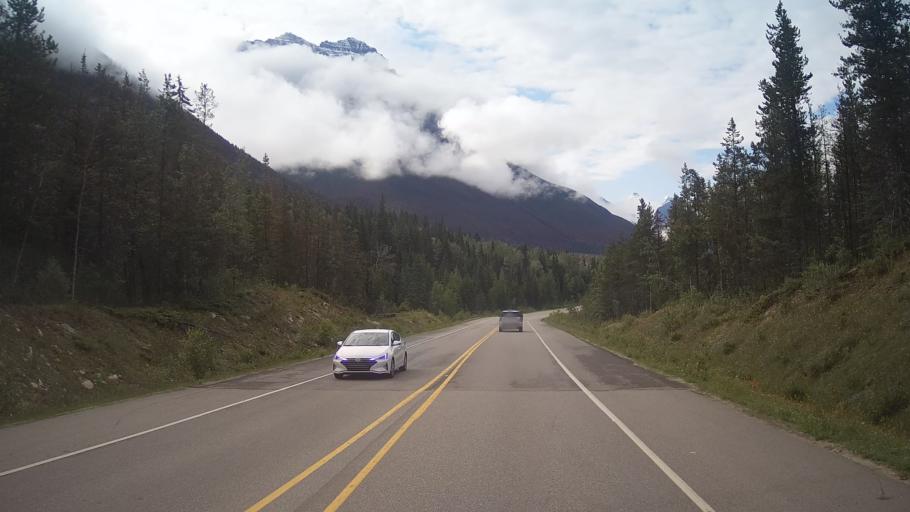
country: CA
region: Alberta
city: Jasper Park Lodge
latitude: 52.6940
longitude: -117.8672
